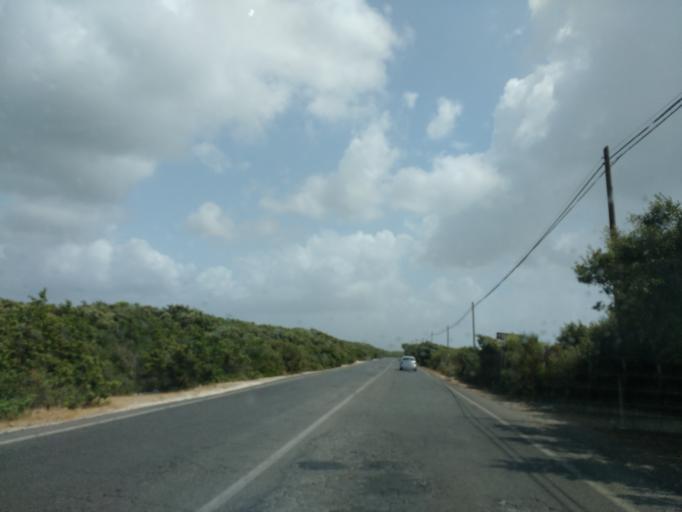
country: IT
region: Latium
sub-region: Citta metropolitana di Roma Capitale
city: Torvaianica
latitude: 41.6818
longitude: 12.3823
